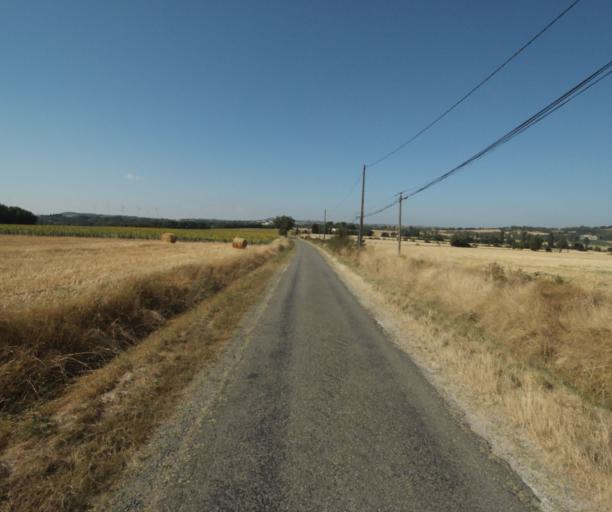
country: FR
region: Midi-Pyrenees
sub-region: Departement de la Haute-Garonne
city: Saint-Felix-Lauragais
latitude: 43.4941
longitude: 1.9250
